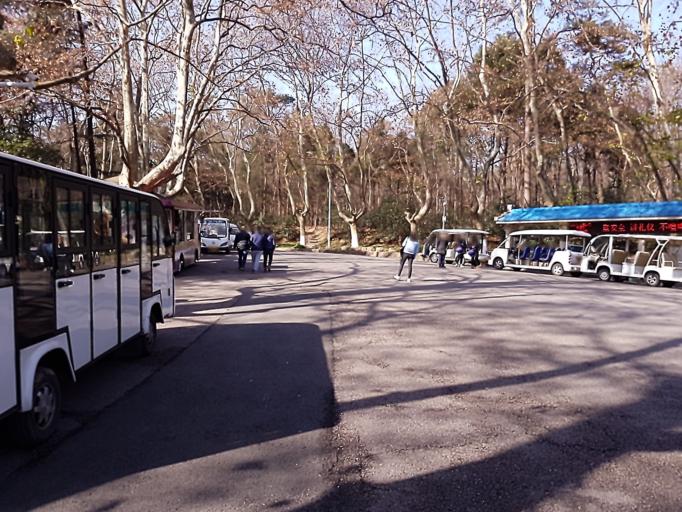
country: CN
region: Jiangsu Sheng
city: Xiaolingwei
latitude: 32.0585
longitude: 118.8480
